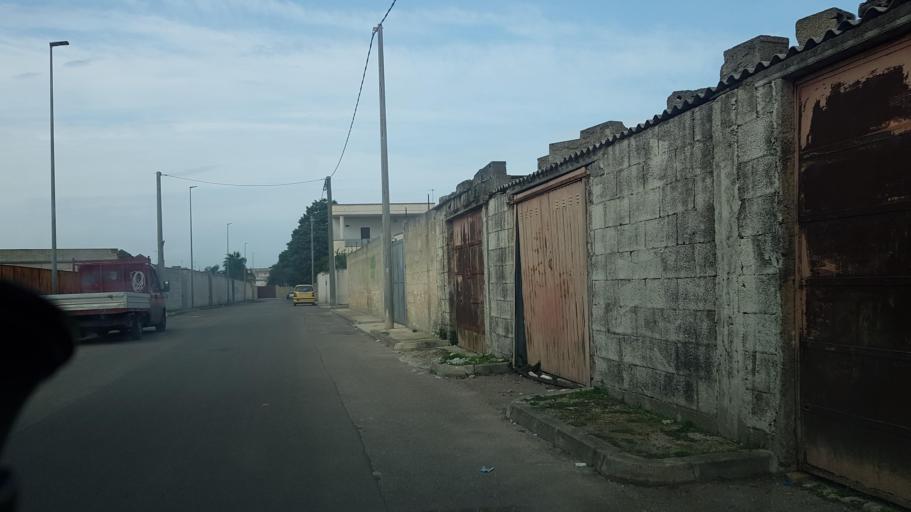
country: IT
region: Apulia
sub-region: Provincia di Lecce
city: Trepuzzi
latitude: 40.4036
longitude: 18.0669
